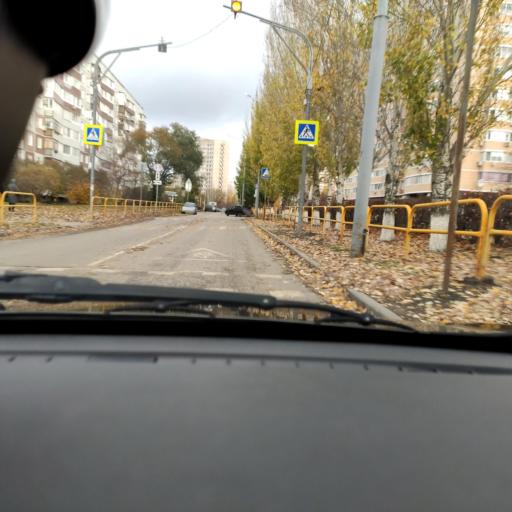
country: RU
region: Samara
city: Tol'yatti
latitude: 53.5399
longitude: 49.3225
